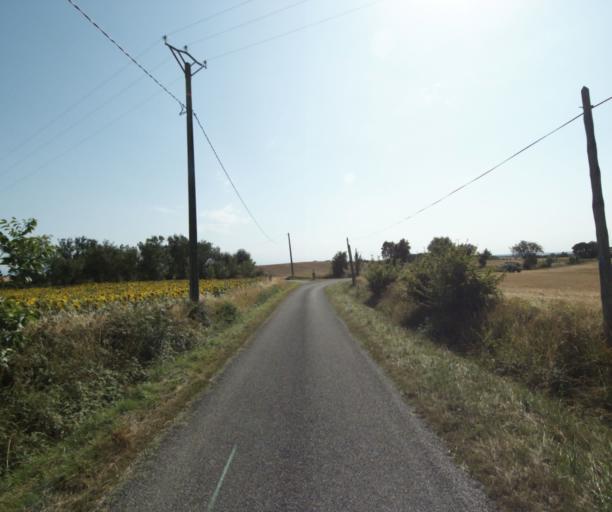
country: FR
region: Midi-Pyrenees
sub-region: Departement de la Haute-Garonne
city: Saint-Felix-Lauragais
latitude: 43.4245
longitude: 1.8387
